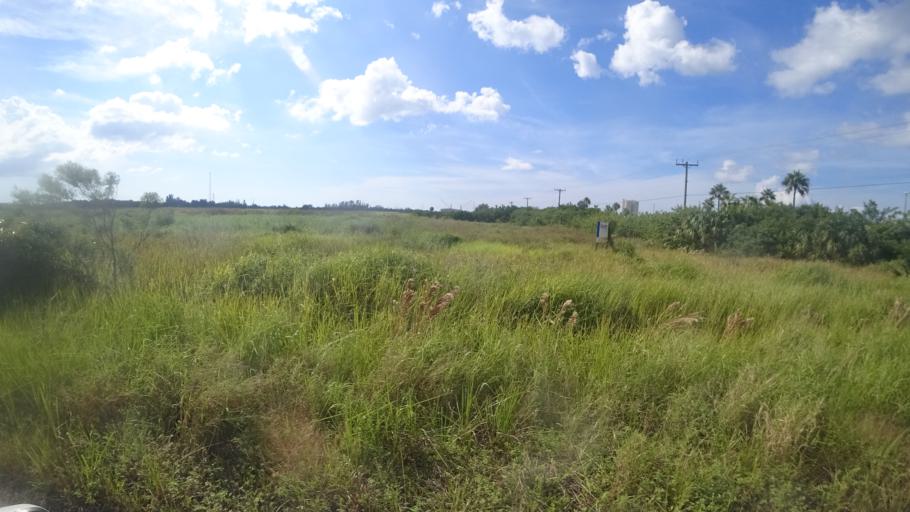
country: US
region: Florida
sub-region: Manatee County
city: Memphis
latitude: 27.6307
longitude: -82.5482
